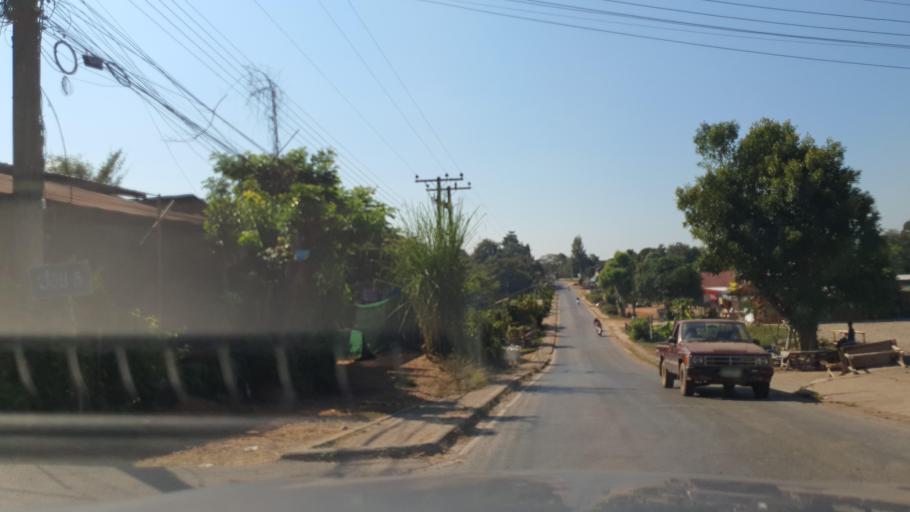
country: TH
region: Nan
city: Pua
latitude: 19.1388
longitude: 100.9332
